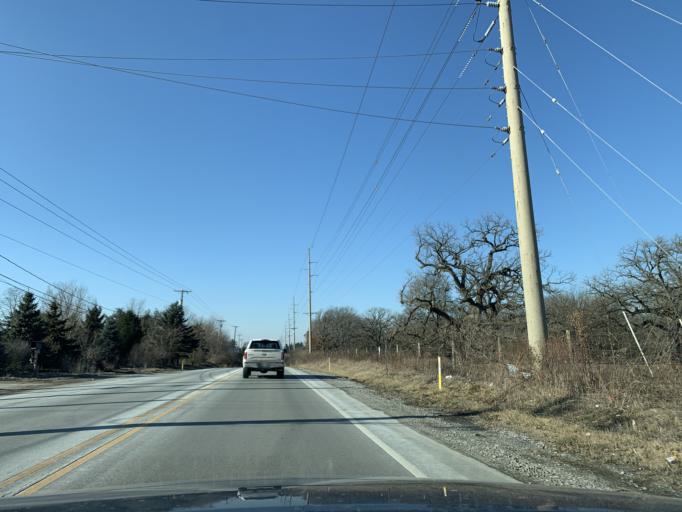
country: US
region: Indiana
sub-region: Lake County
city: Saint John
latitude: 41.4211
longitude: -87.4516
